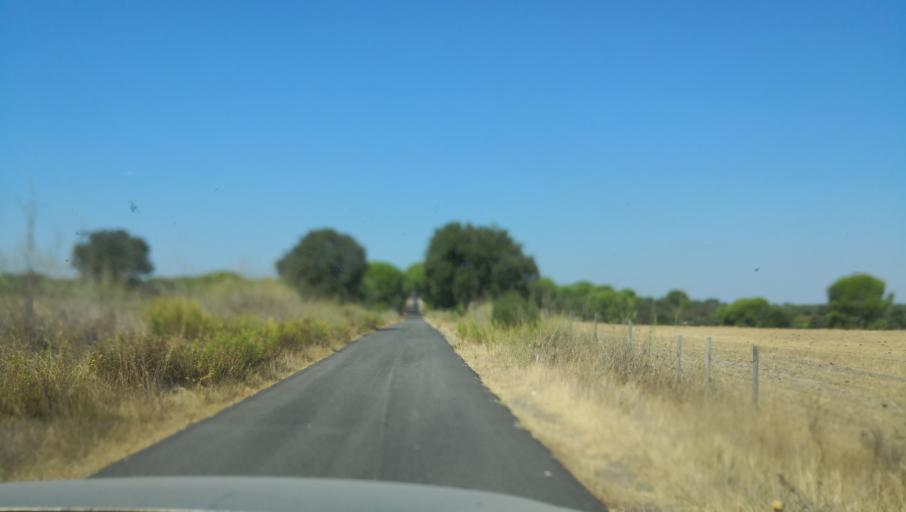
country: PT
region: Setubal
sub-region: Alcacer do Sal
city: Alcacer do Sal
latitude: 38.2550
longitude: -8.3011
